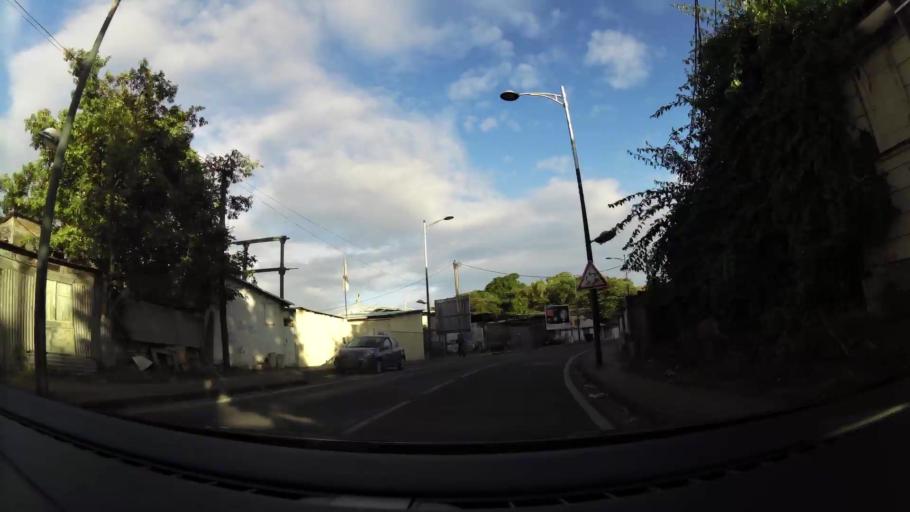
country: GP
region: Guadeloupe
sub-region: Guadeloupe
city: Pointe-a-Pitre
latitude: 16.2280
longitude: -61.5315
